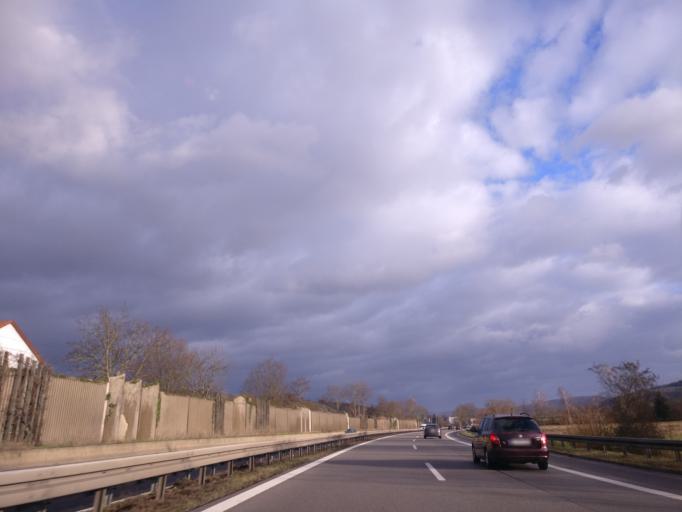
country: DE
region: Baden-Wuerttemberg
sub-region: Regierungsbezirk Stuttgart
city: Winterbach
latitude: 48.8133
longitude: 9.4240
